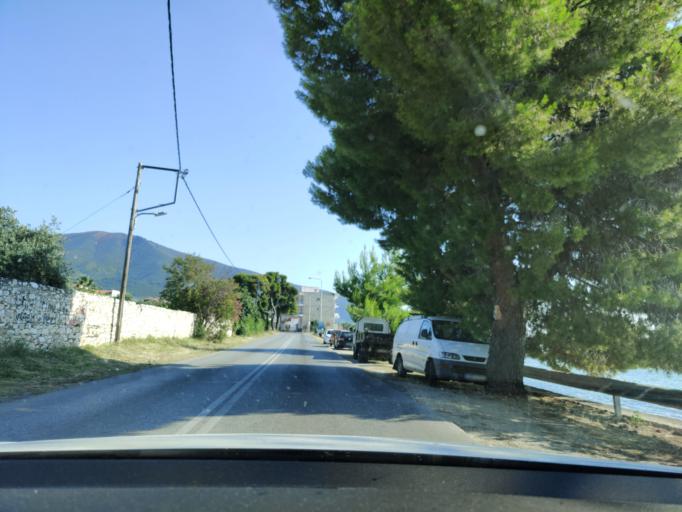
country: GR
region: East Macedonia and Thrace
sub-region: Nomos Kavalas
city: Prinos
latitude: 40.7117
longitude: 24.5340
